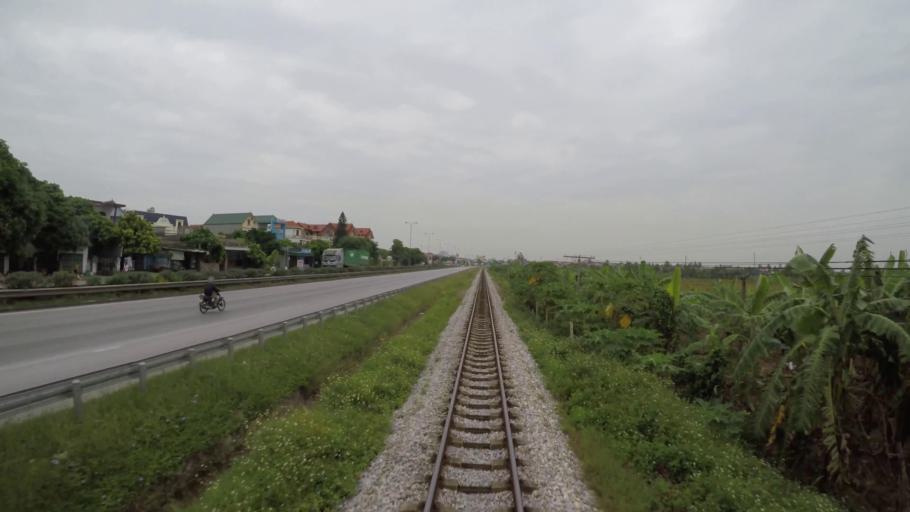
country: VN
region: Hai Duong
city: Phu Thai
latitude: 20.9686
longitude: 106.4536
